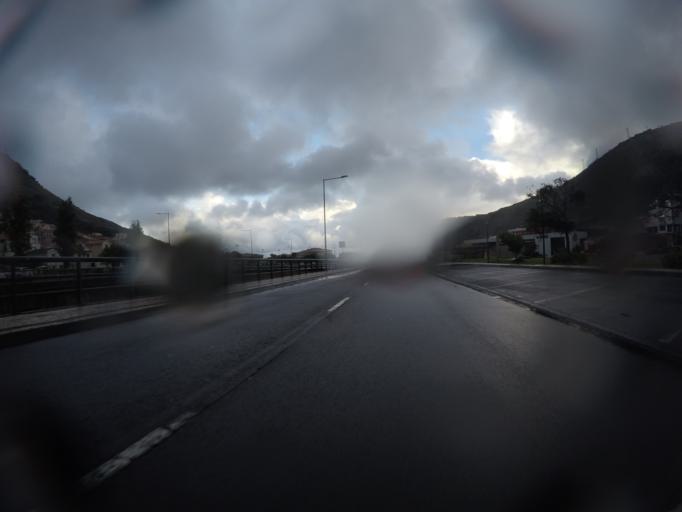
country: PT
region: Madeira
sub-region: Machico
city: Machico
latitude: 32.7222
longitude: -16.7691
